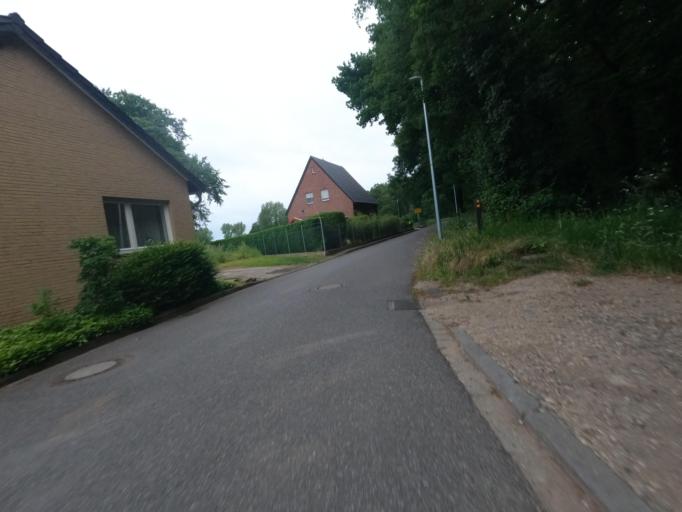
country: DE
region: North Rhine-Westphalia
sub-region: Regierungsbezirk Koln
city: Wassenberg
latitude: 51.1127
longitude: 6.1224
